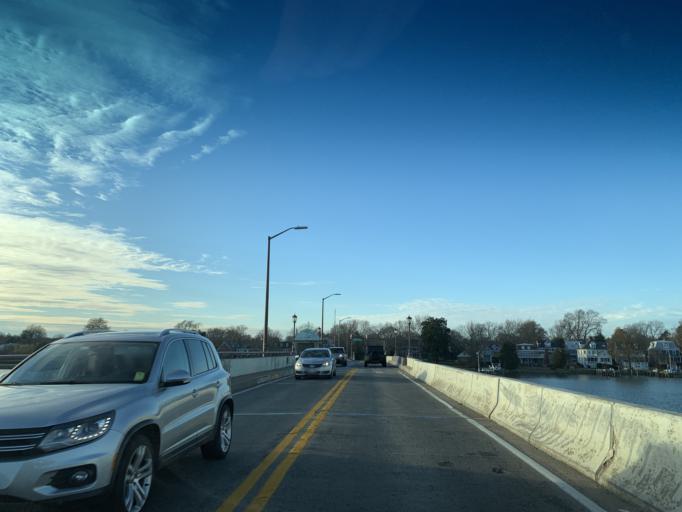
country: US
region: Maryland
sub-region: Kent County
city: Chestertown
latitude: 39.2076
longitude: -76.0596
